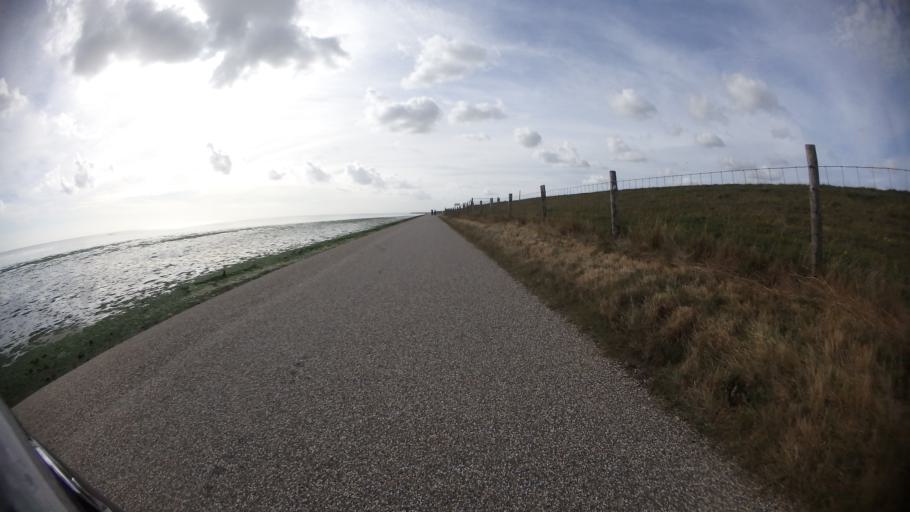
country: NL
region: North Holland
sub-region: Gemeente Texel
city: Den Burg
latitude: 53.1153
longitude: 4.8989
